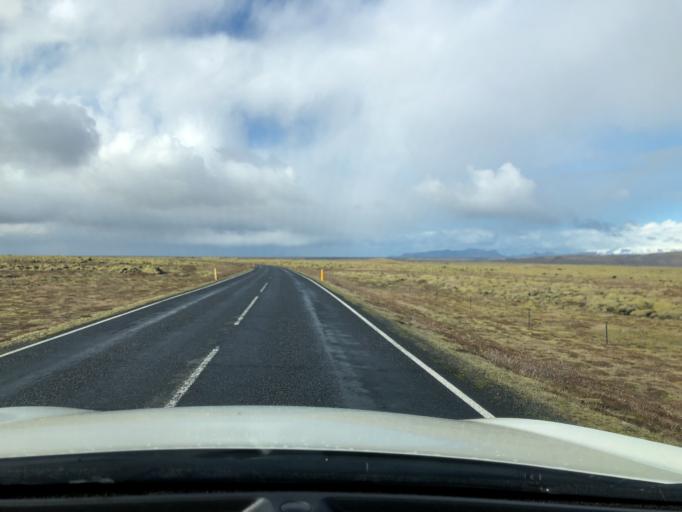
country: IS
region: South
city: Vestmannaeyjar
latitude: 63.6696
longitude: -18.4057
